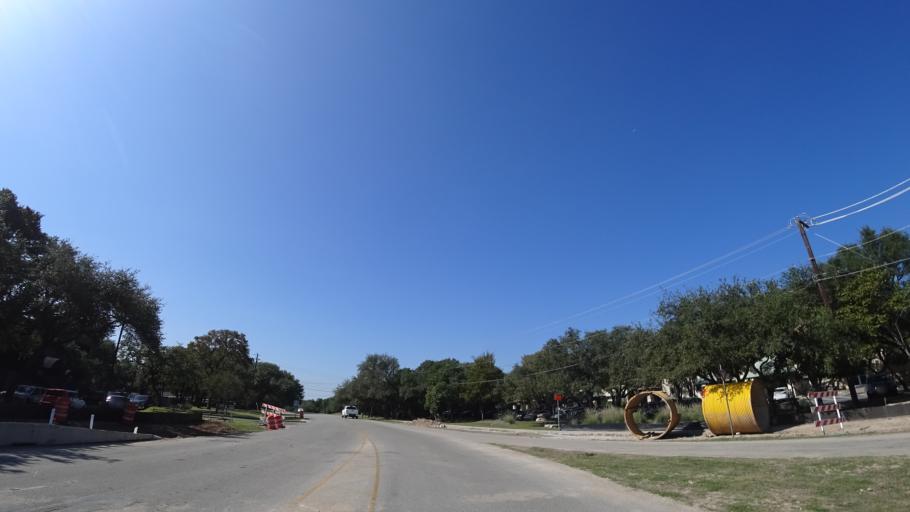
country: US
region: Texas
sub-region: Travis County
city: Rollingwood
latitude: 30.2798
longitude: -97.8075
